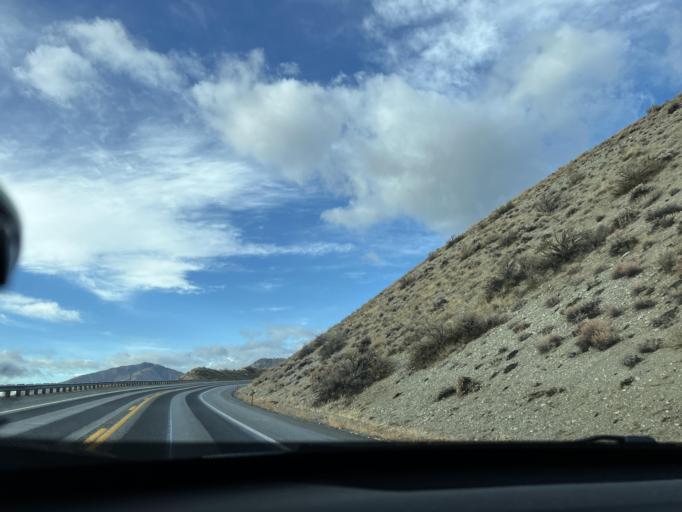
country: US
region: Washington
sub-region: Chelan County
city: Chelan
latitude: 47.8637
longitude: -119.9295
